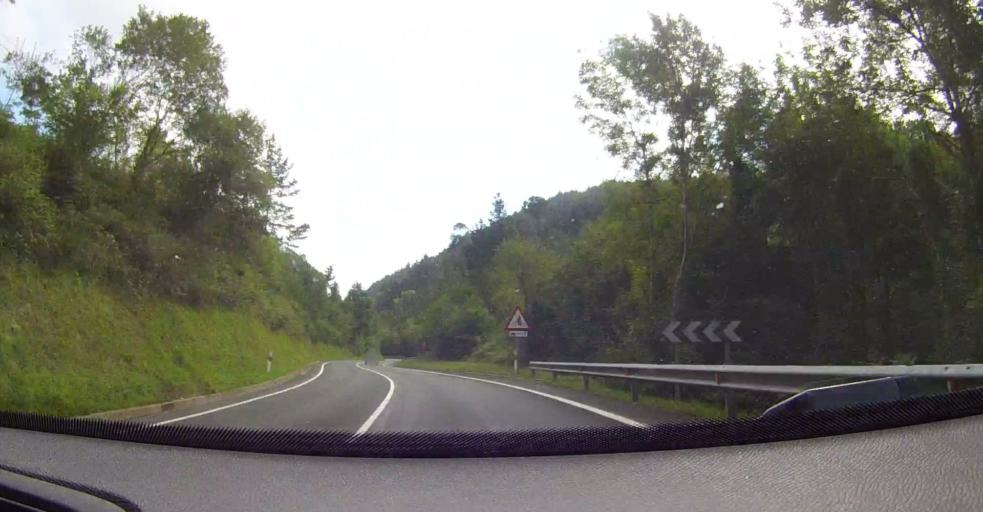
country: ES
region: Basque Country
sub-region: Bizkaia
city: Ibarrangelu
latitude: 43.3776
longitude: -2.6353
